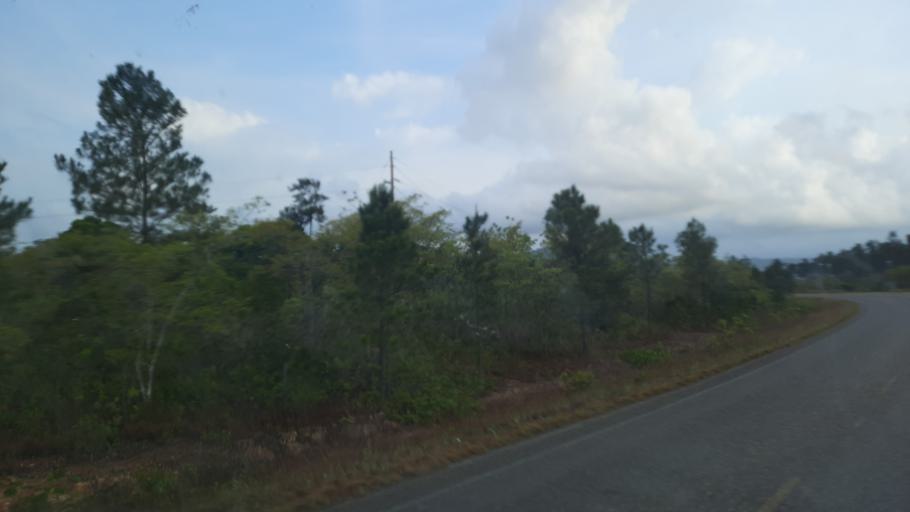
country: BZ
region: Stann Creek
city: Placencia
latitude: 16.6798
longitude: -88.4377
